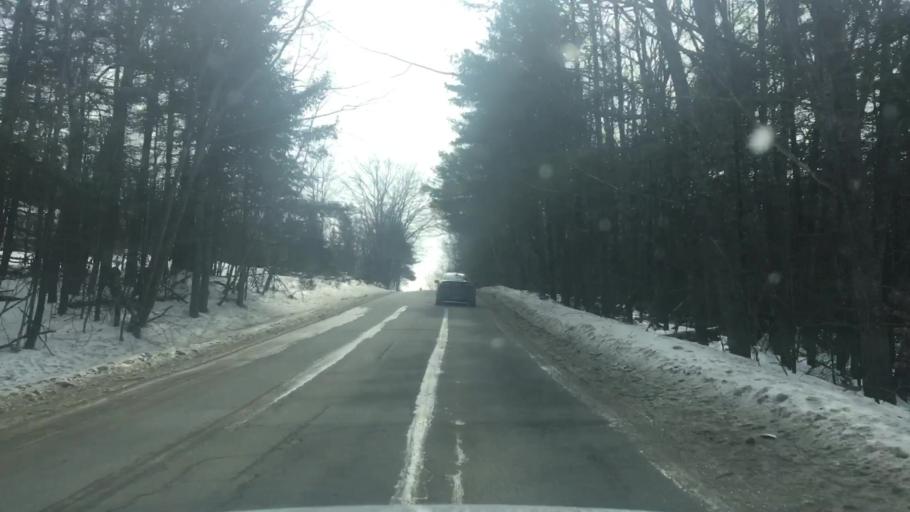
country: US
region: Maine
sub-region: Hancock County
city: Orland
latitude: 44.5897
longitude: -68.7255
